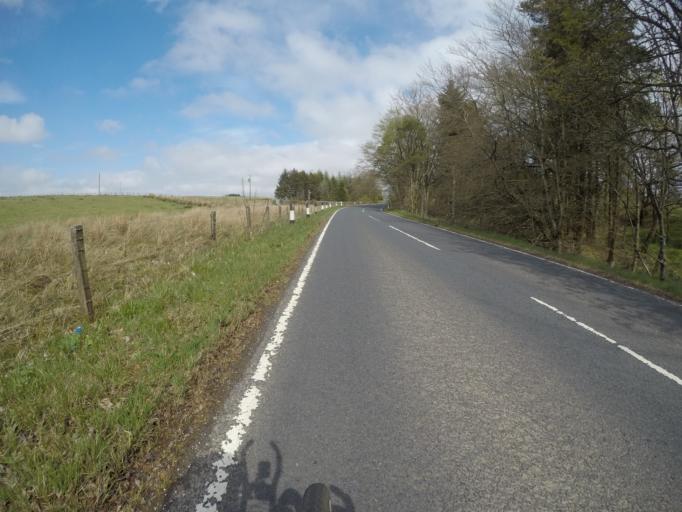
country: GB
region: Scotland
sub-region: East Renfrewshire
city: Neilston
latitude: 55.7191
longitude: -4.4339
